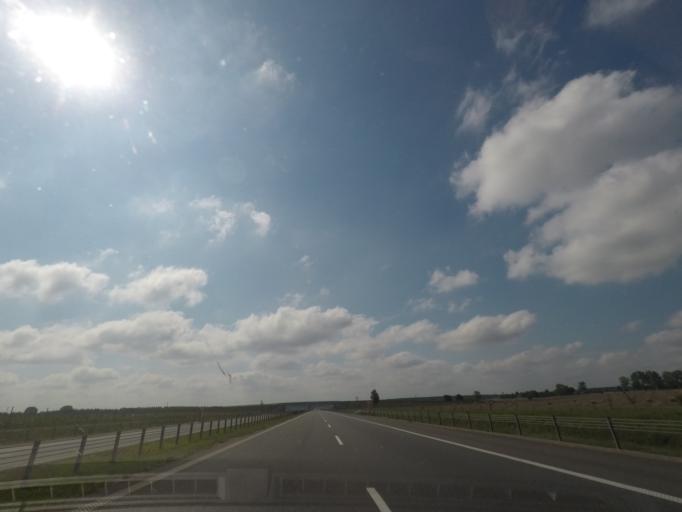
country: PL
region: Kujawsko-Pomorskie
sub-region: Powiat wabrzeski
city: Pluznica
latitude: 53.1745
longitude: 18.7394
